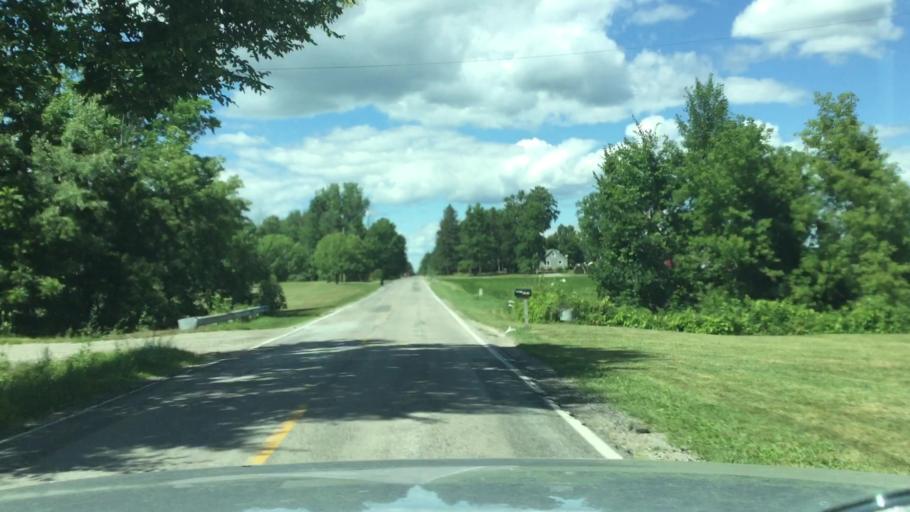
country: US
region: Michigan
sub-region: Saginaw County
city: Hemlock
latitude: 43.3716
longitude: -84.1902
